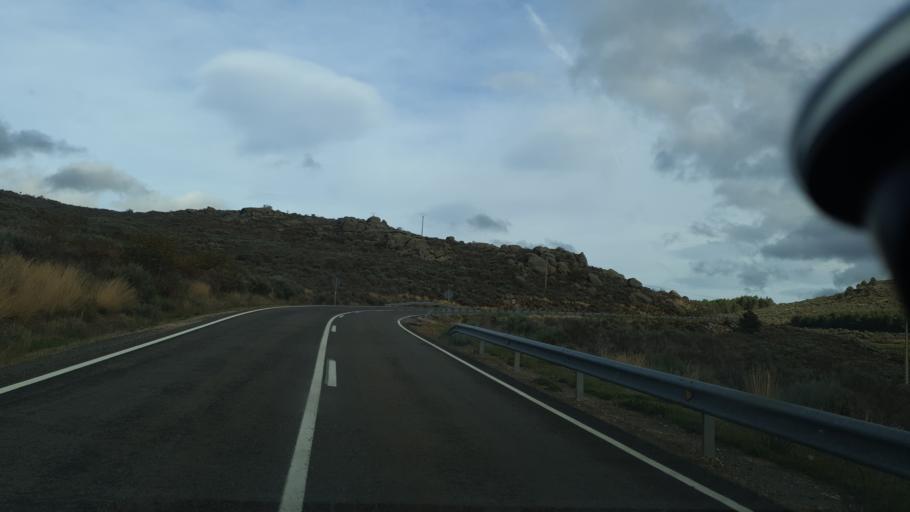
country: ES
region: Castille and Leon
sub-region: Provincia de Avila
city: Hoyocasero
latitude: 40.3897
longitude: -5.0084
